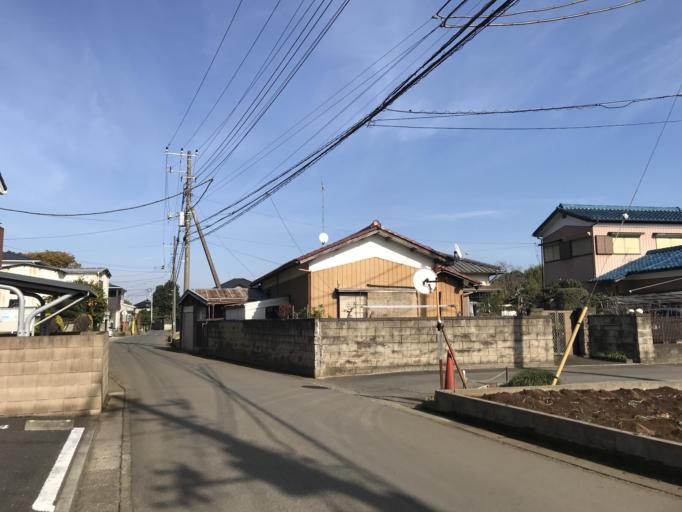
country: JP
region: Chiba
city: Shiroi
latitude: 35.7853
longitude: 139.9949
